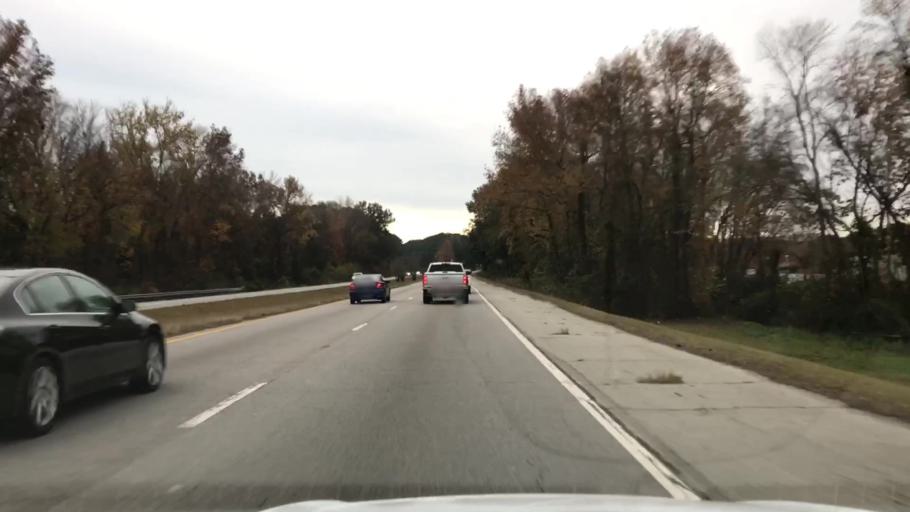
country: US
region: South Carolina
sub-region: Berkeley County
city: Hanahan
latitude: 32.9433
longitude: -80.0484
